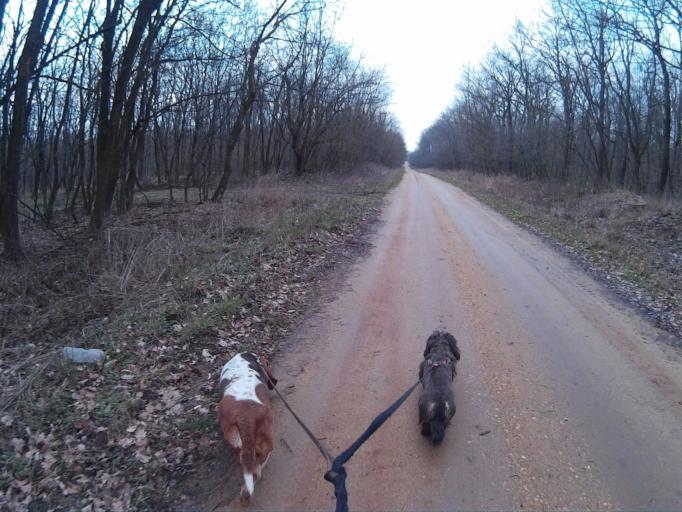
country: HU
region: Vas
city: Janoshaza
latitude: 47.1247
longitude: 17.0503
